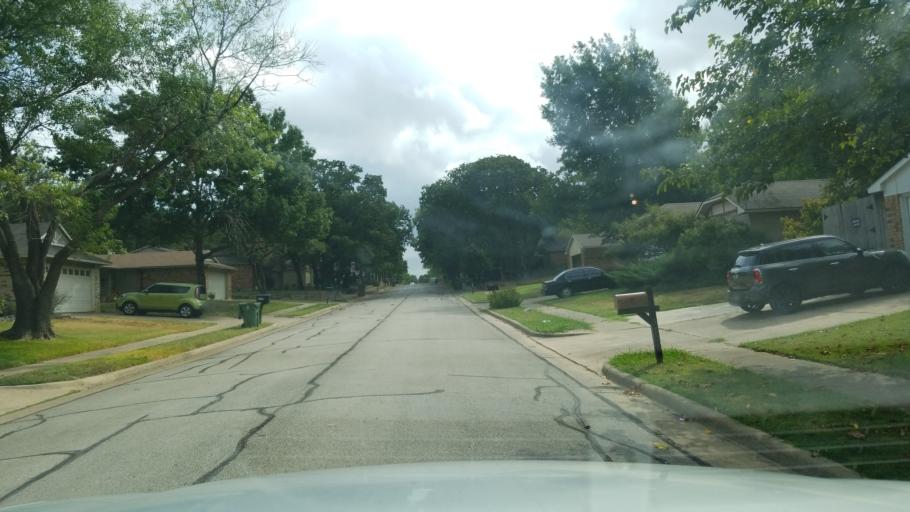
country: US
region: Texas
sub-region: Tarrant County
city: Euless
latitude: 32.8491
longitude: -97.1086
